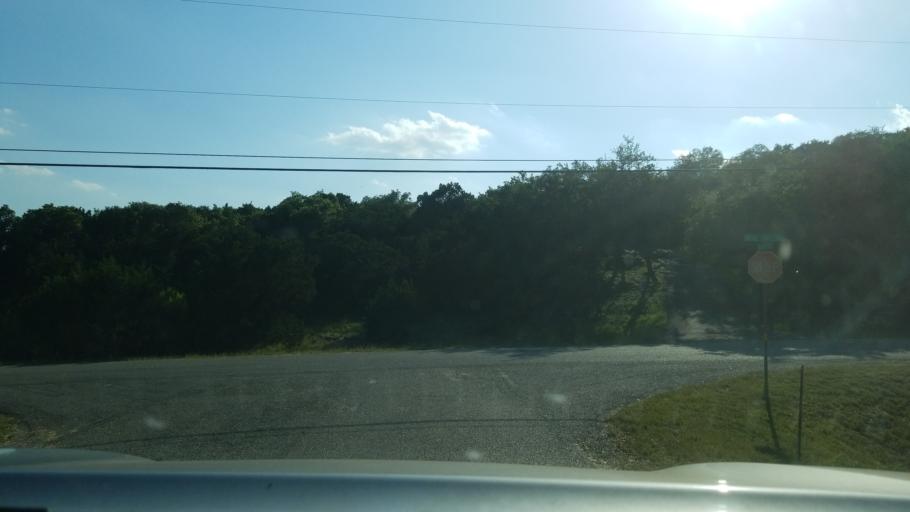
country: US
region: Texas
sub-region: Comal County
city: Bulverde
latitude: 29.7766
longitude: -98.4424
